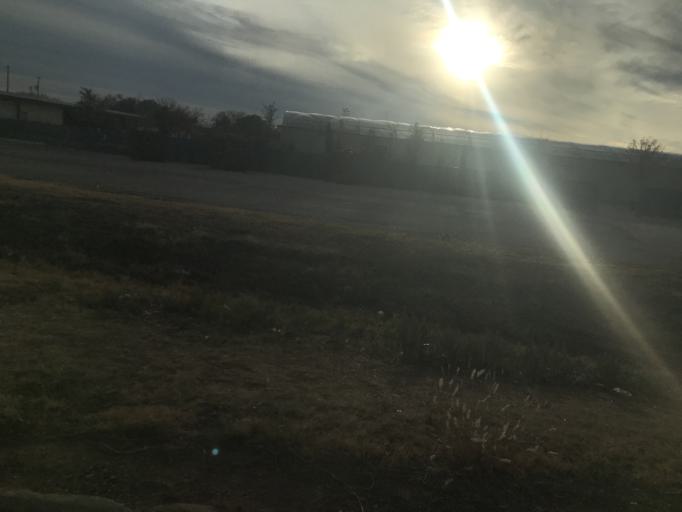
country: US
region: Texas
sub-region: Taylor County
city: Abilene
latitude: 32.4159
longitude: -99.7791
